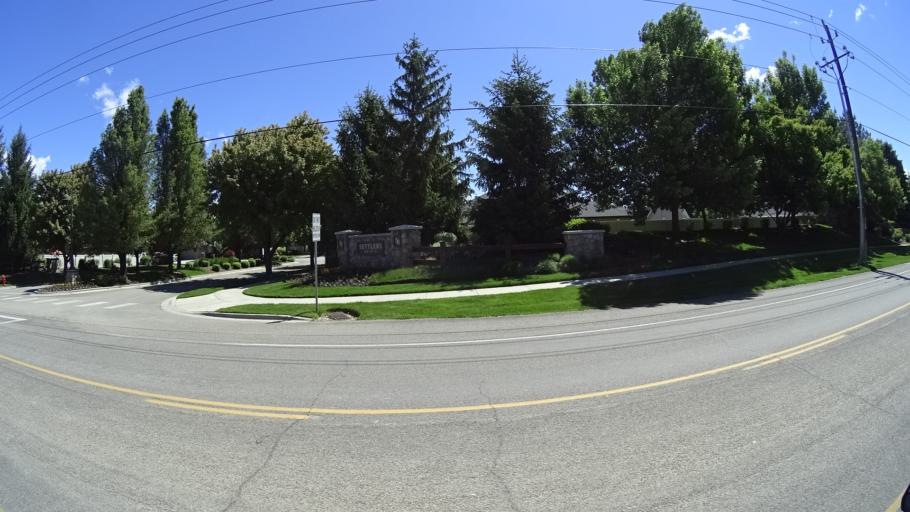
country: US
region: Idaho
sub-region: Ada County
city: Meridian
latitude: 43.6462
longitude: -116.3746
